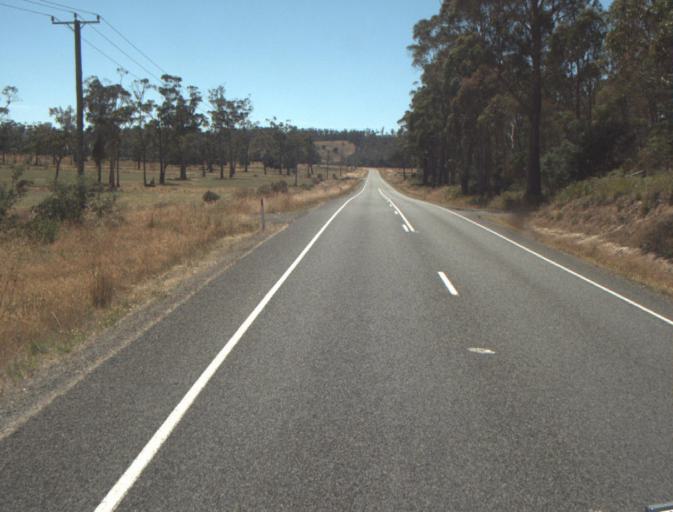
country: AU
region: Tasmania
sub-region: Launceston
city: Newstead
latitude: -41.3666
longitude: 147.3295
